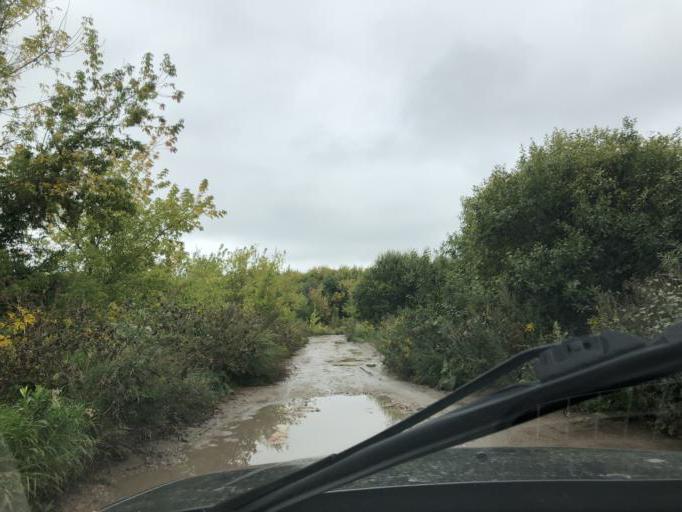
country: RU
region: Tula
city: Mendeleyevskiy
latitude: 54.1679
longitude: 37.5507
